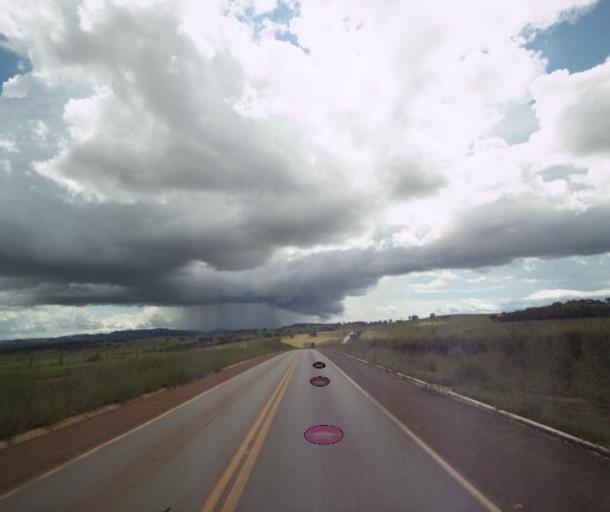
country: BR
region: Goias
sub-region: Uruacu
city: Uruacu
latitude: -14.6898
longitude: -49.1231
